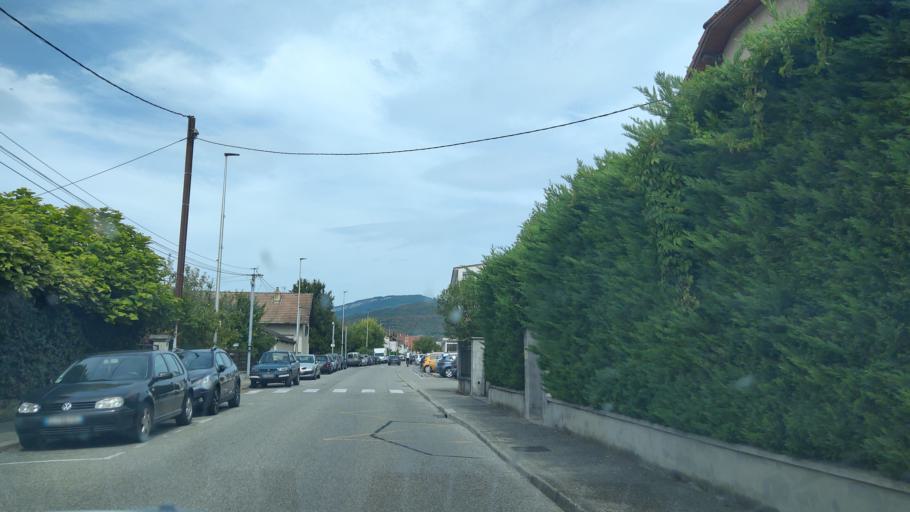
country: FR
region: Rhone-Alpes
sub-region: Departement de la Savoie
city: Tresserve
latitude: 45.6873
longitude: 5.9076
